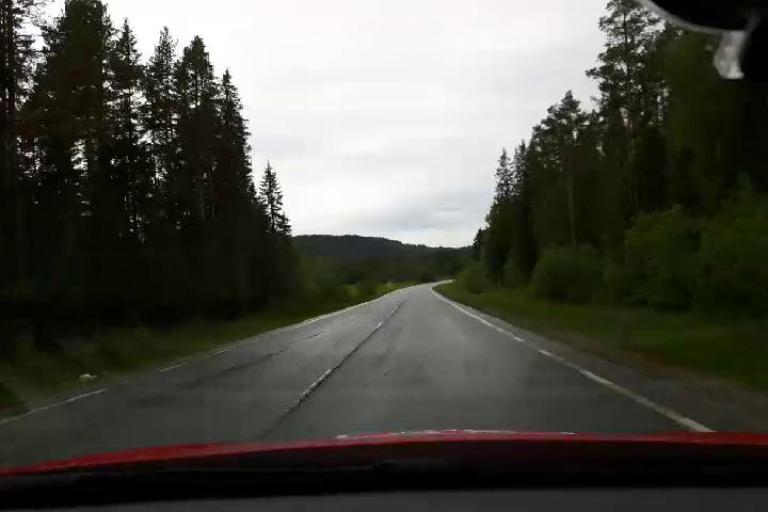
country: SE
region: Jaemtland
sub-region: Bergs Kommun
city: Hoverberg
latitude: 62.9046
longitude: 14.3375
